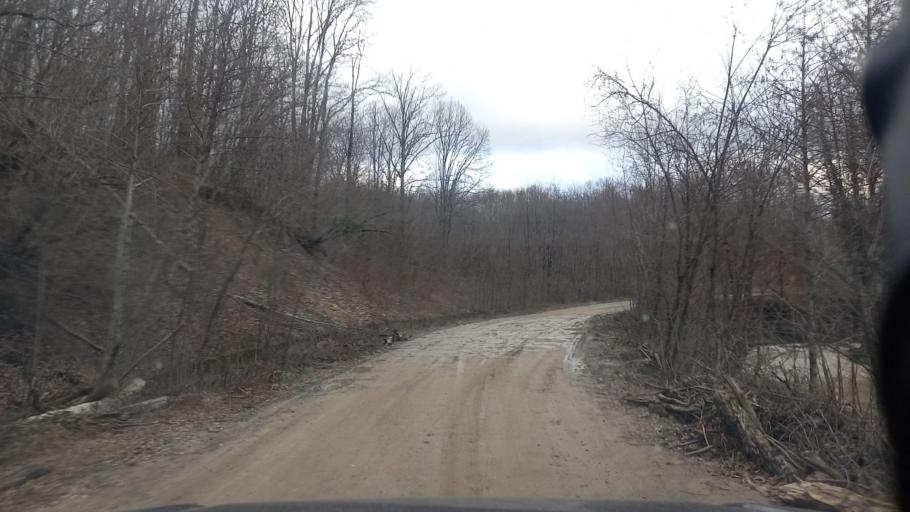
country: RU
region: Krasnodarskiy
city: Dzhubga
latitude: 44.4845
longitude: 38.7884
